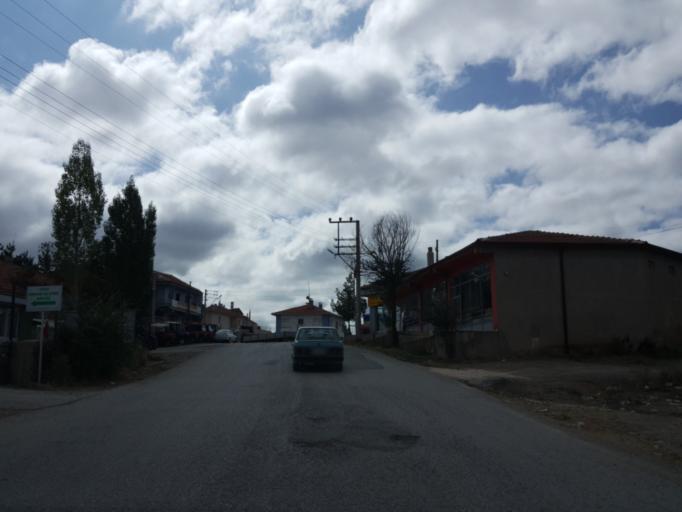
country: TR
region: Sivas
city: Yavu
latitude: 39.7938
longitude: 36.2039
